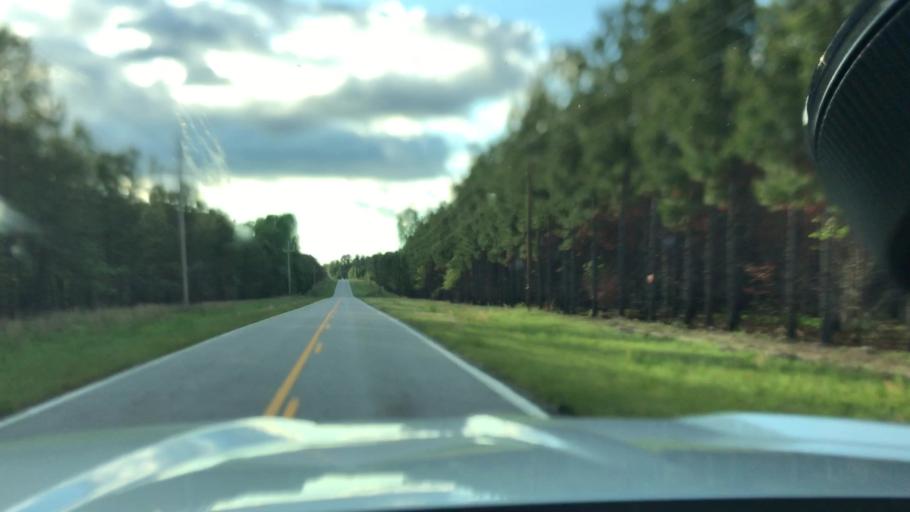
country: US
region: South Carolina
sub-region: Bamberg County
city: Denmark
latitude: 33.4700
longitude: -81.1675
